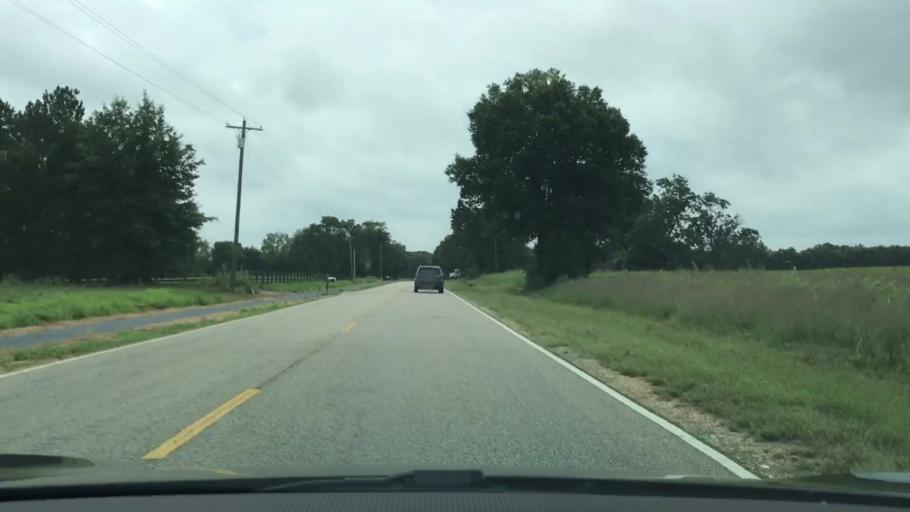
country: US
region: Alabama
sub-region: Montgomery County
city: Pike Road
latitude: 32.3018
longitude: -86.0672
